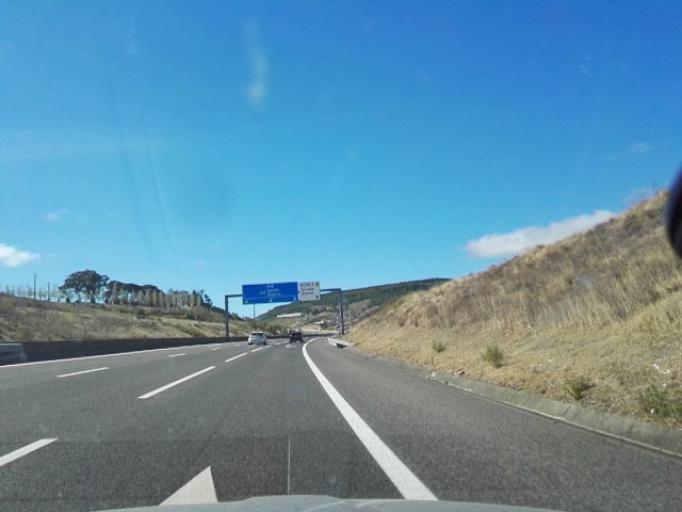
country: PT
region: Lisbon
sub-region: Arruda Dos Vinhos
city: Arruda dos Vinhos
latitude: 38.9726
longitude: -9.0599
